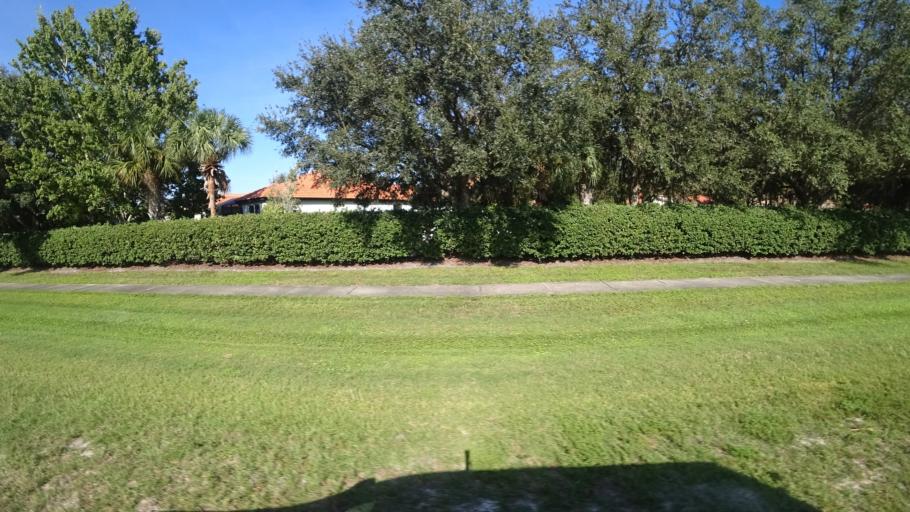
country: US
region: Florida
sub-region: Sarasota County
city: Desoto Lakes
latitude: 27.4186
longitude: -82.4632
